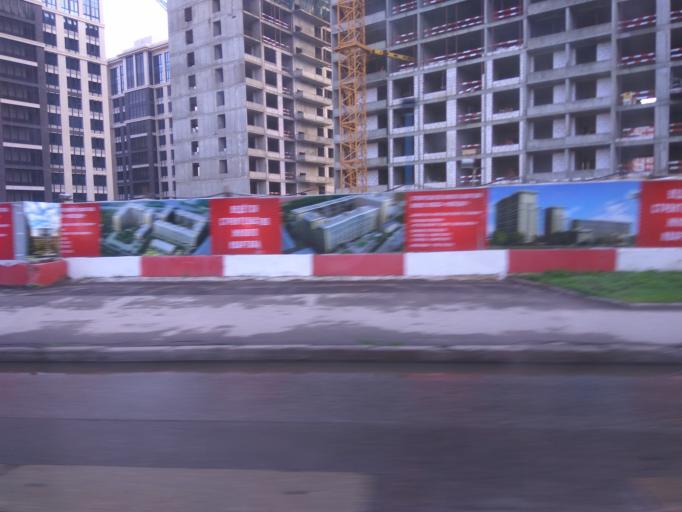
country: RU
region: Moskovskaya
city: Bogorodskoye
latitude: 55.8010
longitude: 37.7116
